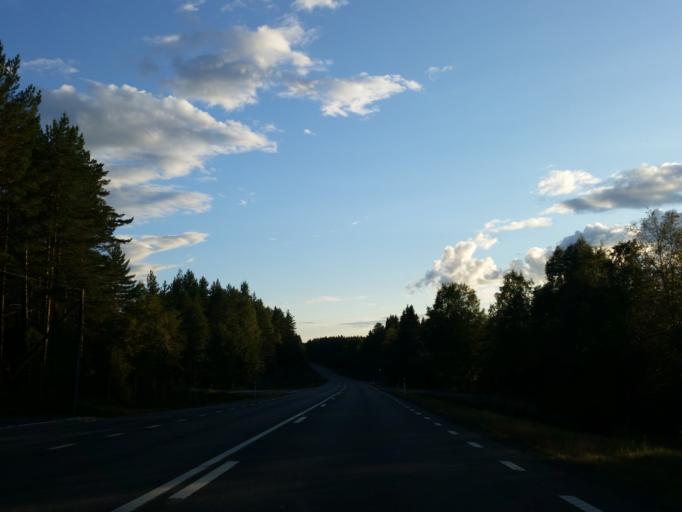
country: SE
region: Vaesterbotten
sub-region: Robertsfors Kommun
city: Robertsfors
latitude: 64.0142
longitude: 20.8222
